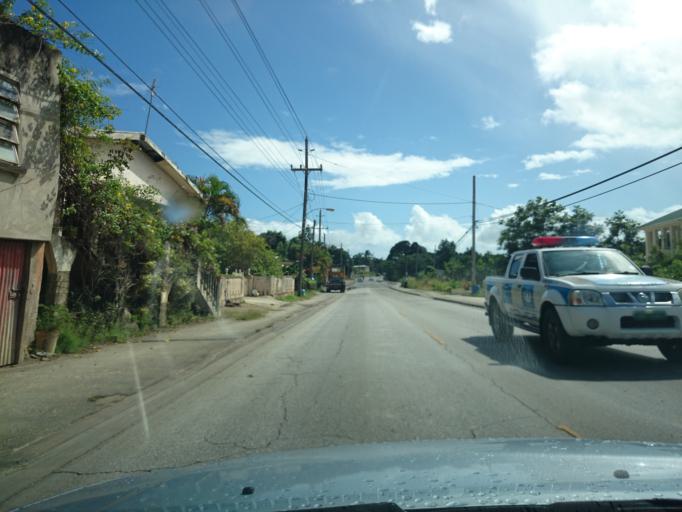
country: BB
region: Saint Peter
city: Speightstown
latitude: 13.2254
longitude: -59.6221
